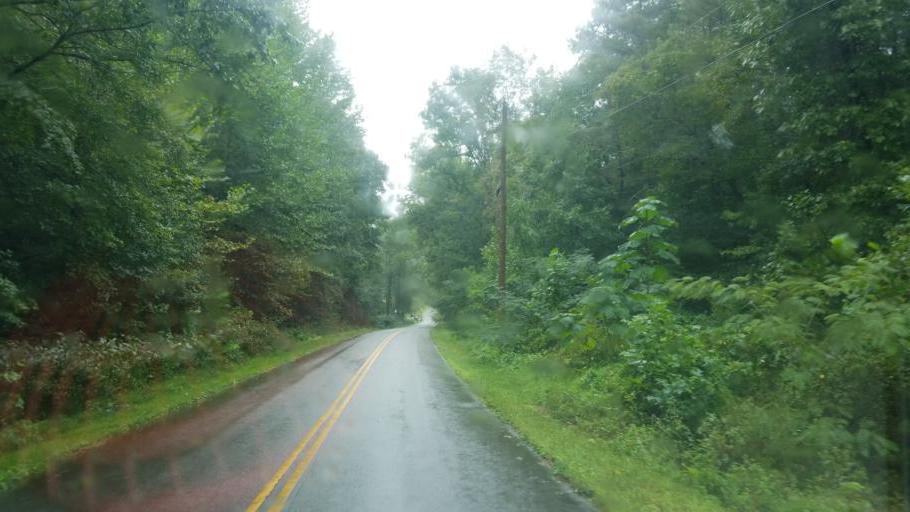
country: US
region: Ohio
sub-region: Scioto County
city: West Portsmouth
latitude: 38.7571
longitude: -83.1036
